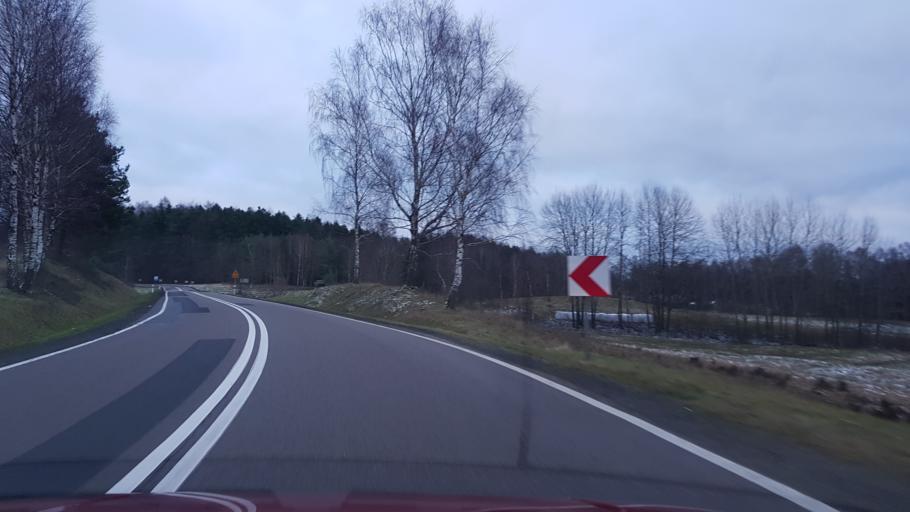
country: PL
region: Pomeranian Voivodeship
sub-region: Powiat bytowski
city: Tuchomie
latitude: 54.0648
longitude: 17.2646
